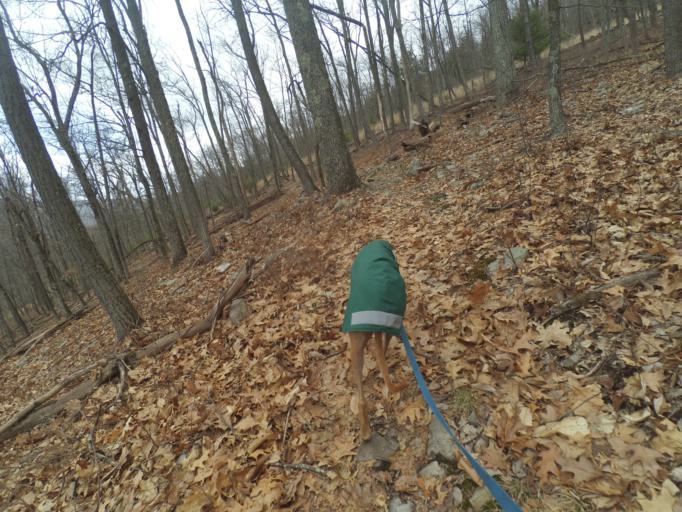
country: US
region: Pennsylvania
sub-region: Centre County
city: Boalsburg
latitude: 40.7631
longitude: -77.7099
